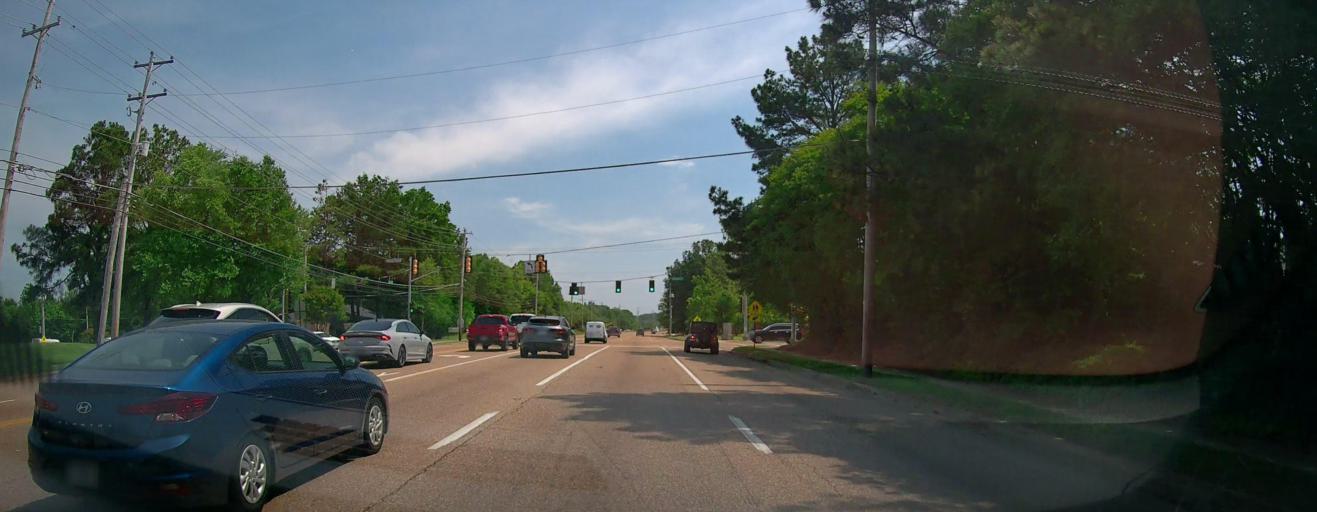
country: US
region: Tennessee
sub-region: Shelby County
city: Germantown
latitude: 35.0288
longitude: -89.7959
